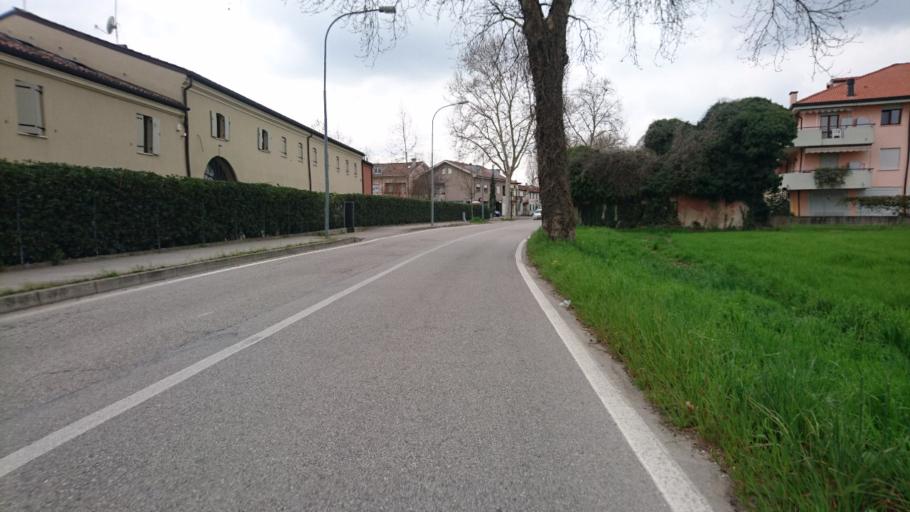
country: IT
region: Veneto
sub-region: Provincia di Padova
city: Vigodarzere
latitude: 45.4511
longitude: 11.8671
